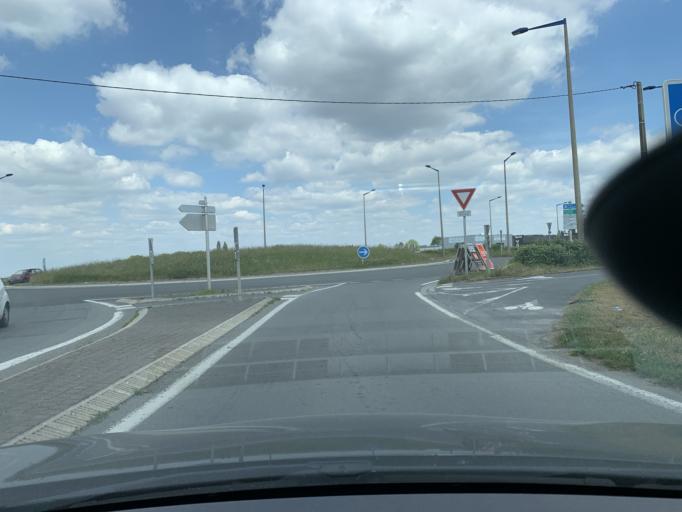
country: FR
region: Nord-Pas-de-Calais
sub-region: Departement du Nord
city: Goeulzin
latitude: 50.3377
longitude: 3.0945
